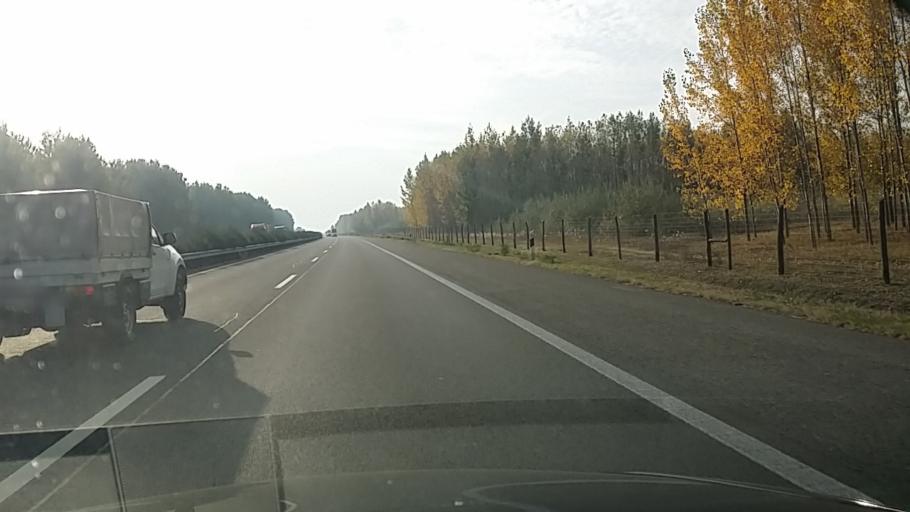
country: HU
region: Csongrad
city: Csengele
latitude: 46.6001
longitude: 19.8467
